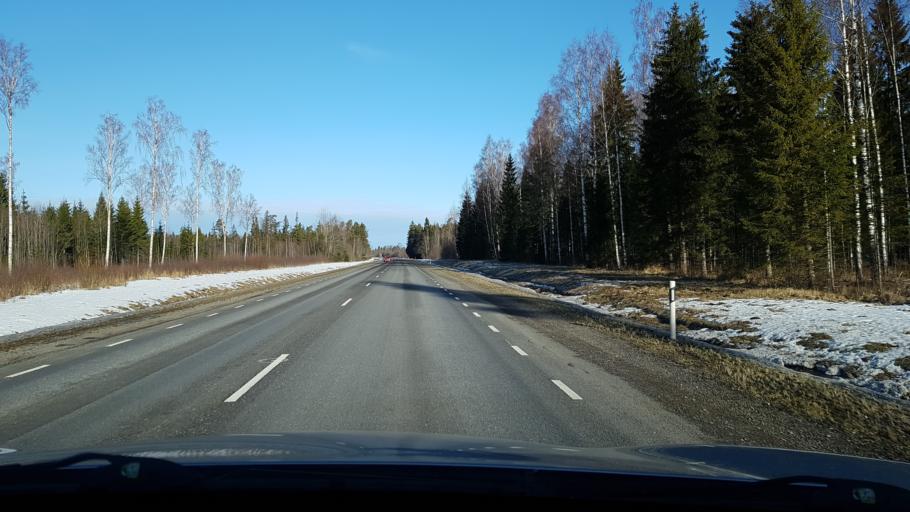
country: EE
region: Viljandimaa
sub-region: Vohma linn
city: Vohma
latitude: 58.6070
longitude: 25.5723
